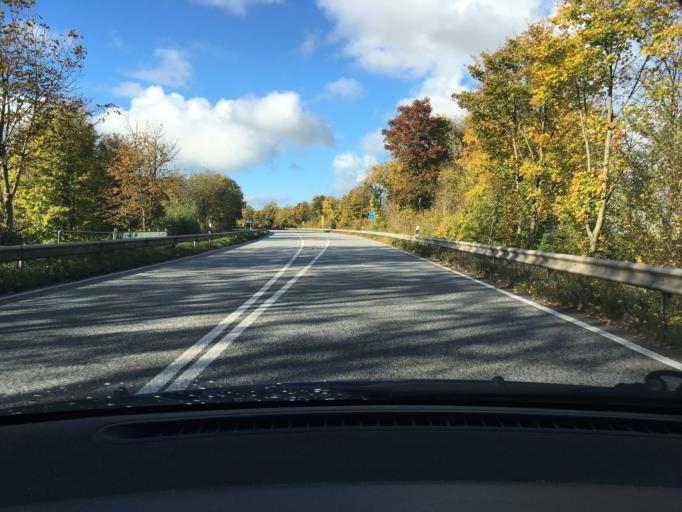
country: DE
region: Schleswig-Holstein
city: Busdorf
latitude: 54.4824
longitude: 9.5408
